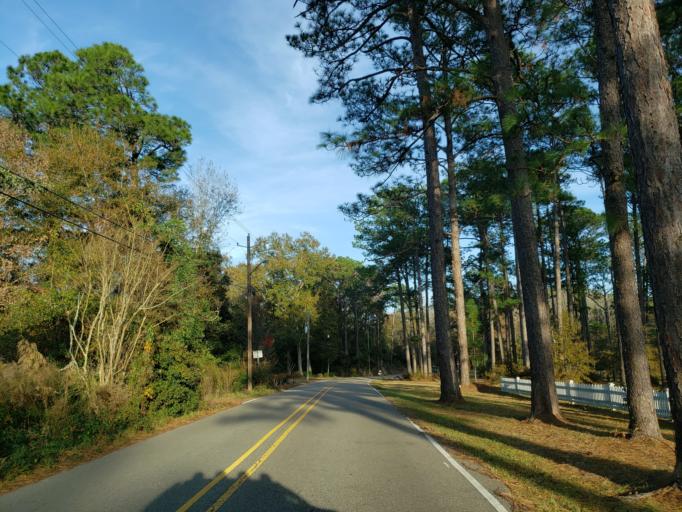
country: US
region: Mississippi
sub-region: Lamar County
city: West Hattiesburg
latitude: 31.2965
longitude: -89.3330
